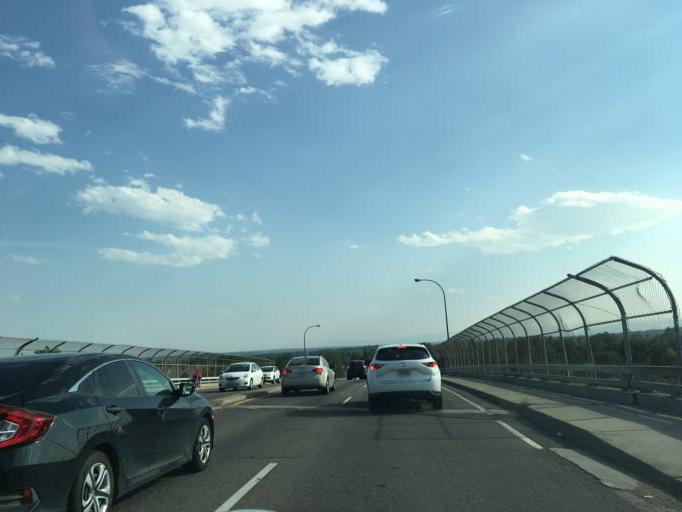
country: US
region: Colorado
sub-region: Adams County
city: Westminster
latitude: 39.8525
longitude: -105.0528
